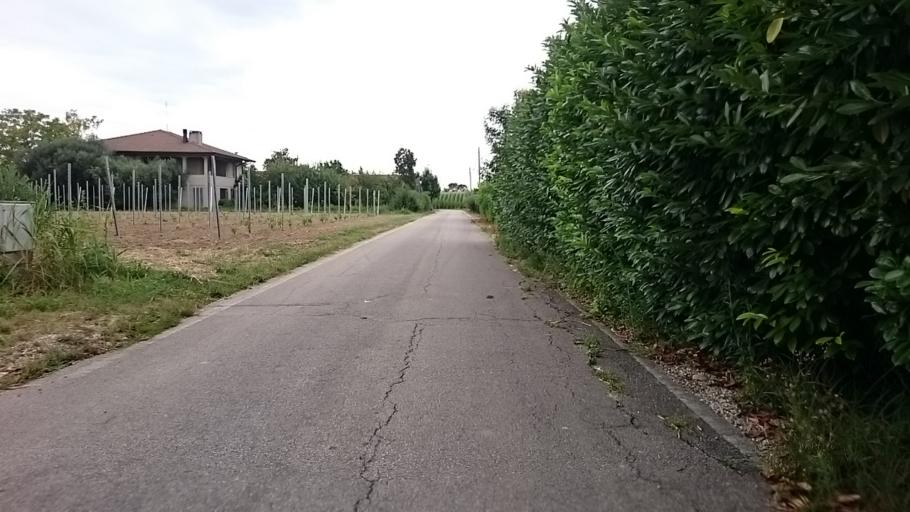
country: IT
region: Veneto
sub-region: Provincia di Padova
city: Terradura
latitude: 45.3228
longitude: 11.8386
